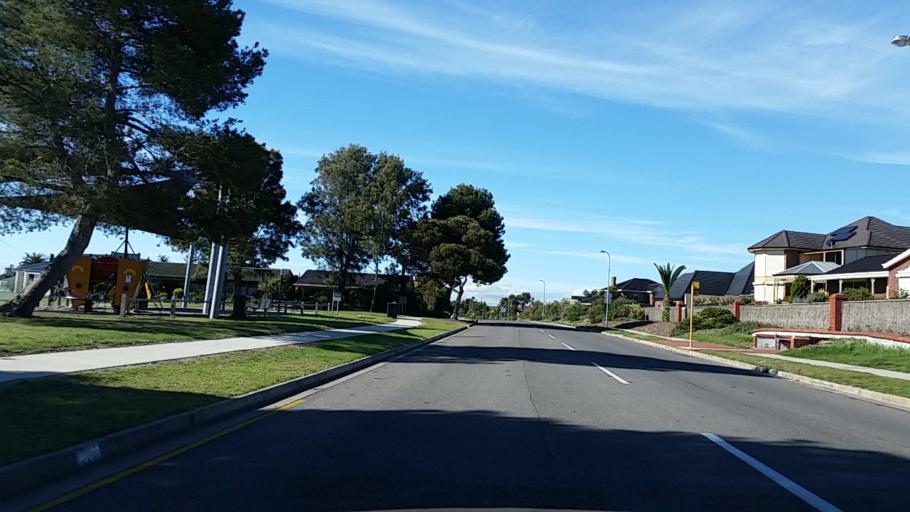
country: AU
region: South Australia
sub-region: Charles Sturt
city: West Lakes Shore
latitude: -34.8658
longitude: 138.4910
